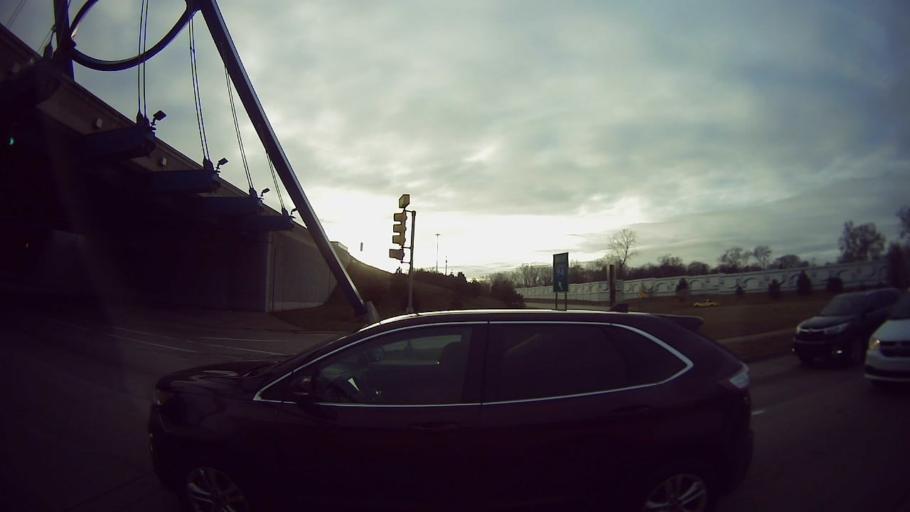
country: US
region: Michigan
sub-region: Wayne County
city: Taylor
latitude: 42.2651
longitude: -83.2706
